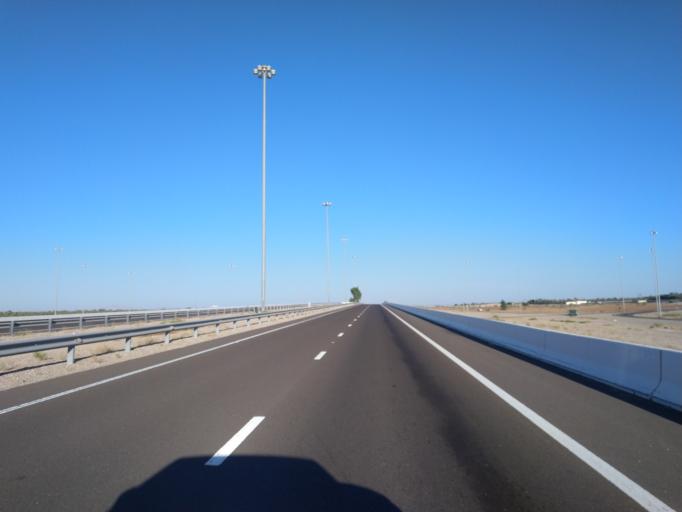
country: OM
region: Al Buraimi
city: Al Buraymi
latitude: 24.5380
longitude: 55.6010
